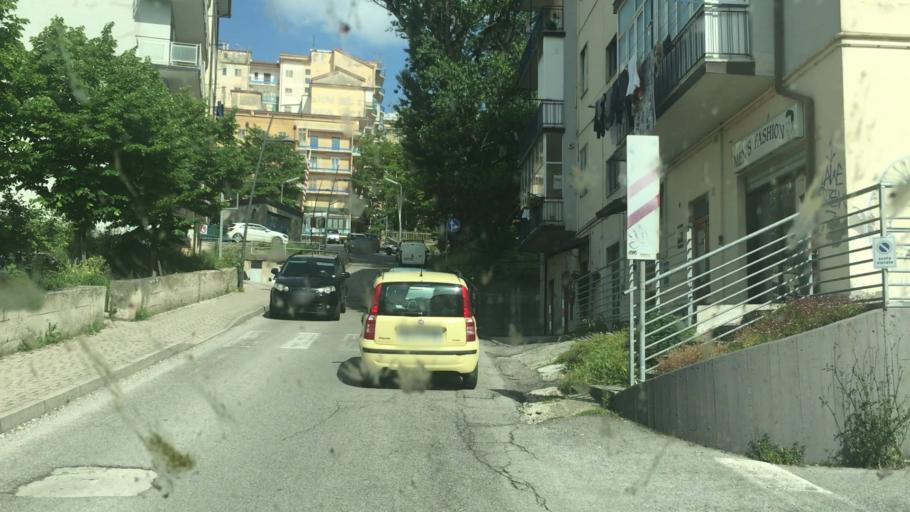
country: IT
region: Basilicate
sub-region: Provincia di Potenza
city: Potenza
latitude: 40.6422
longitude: 15.8024
